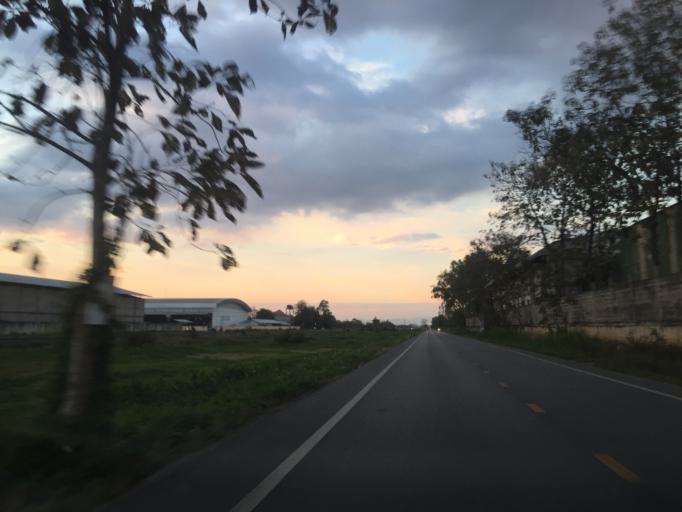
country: TH
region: Lamphun
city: Lamphun
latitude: 18.5591
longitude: 99.0429
